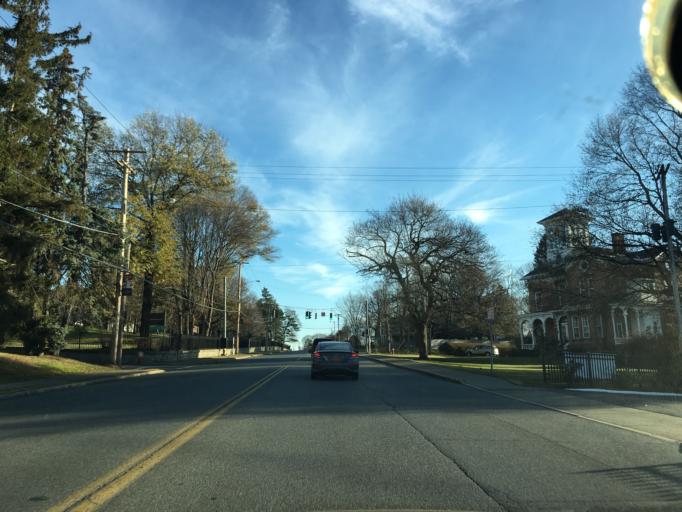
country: US
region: New York
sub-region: Rensselaer County
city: Wynantskill
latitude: 42.7130
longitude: -73.6664
